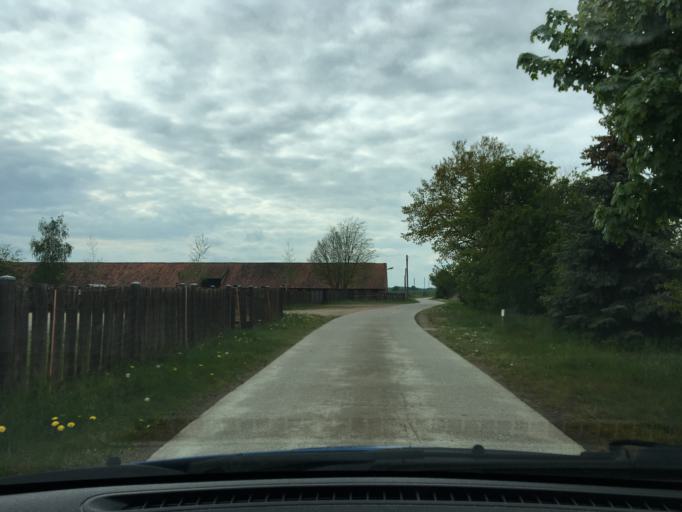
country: DE
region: Lower Saxony
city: Neu Darchau
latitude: 53.2810
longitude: 10.9180
